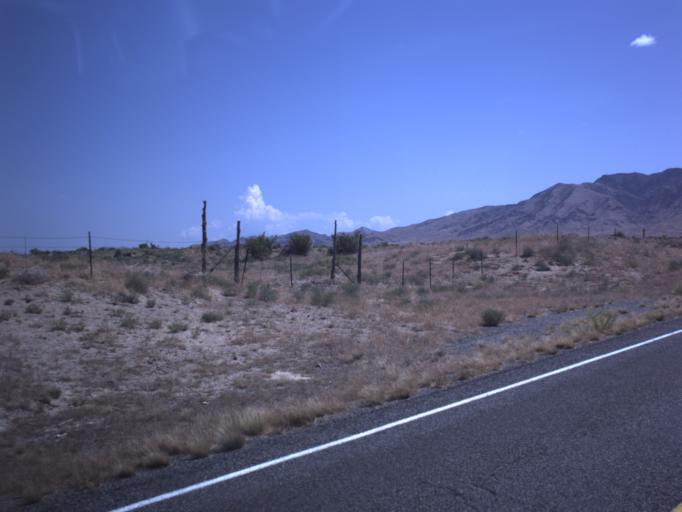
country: US
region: Utah
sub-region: Millard County
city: Delta
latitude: 39.3547
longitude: -112.3866
